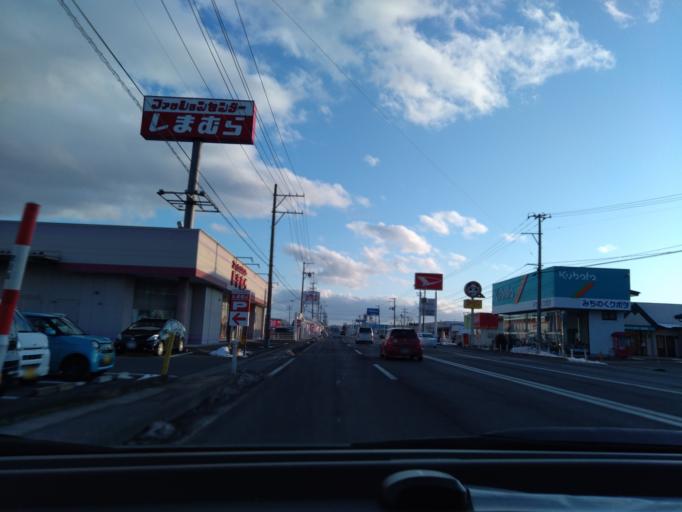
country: JP
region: Iwate
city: Morioka-shi
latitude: 39.5477
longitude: 141.1681
